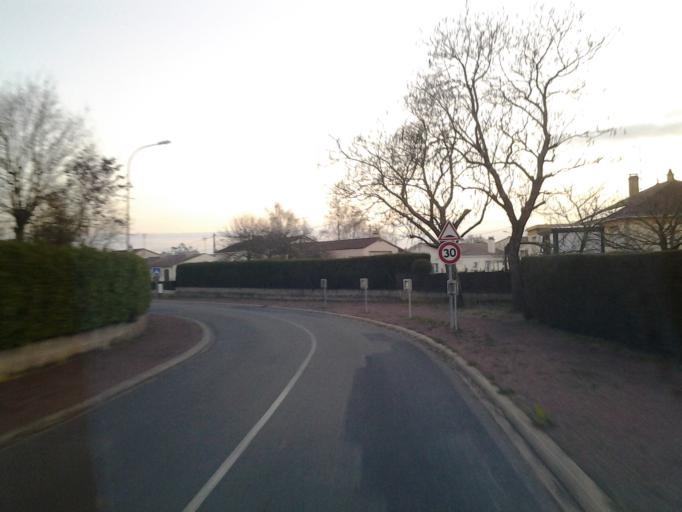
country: FR
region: Pays de la Loire
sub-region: Departement de la Vendee
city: Mouilleron-le-Captif
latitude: 46.7164
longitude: -1.4499
